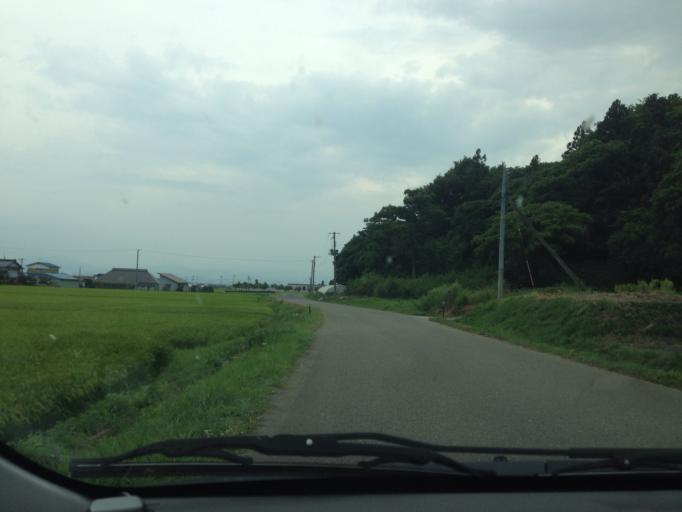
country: JP
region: Fukushima
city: Kitakata
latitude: 37.6518
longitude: 139.8454
